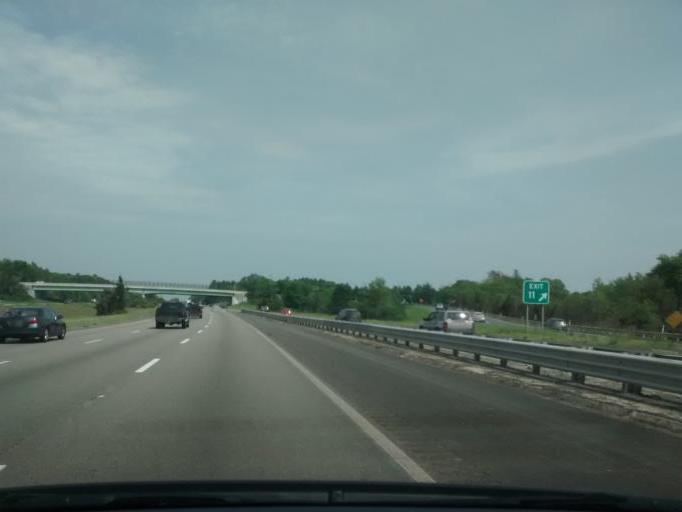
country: US
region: Massachusetts
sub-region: Bristol County
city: Mansfield Center
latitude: 42.0013
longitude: -71.2147
